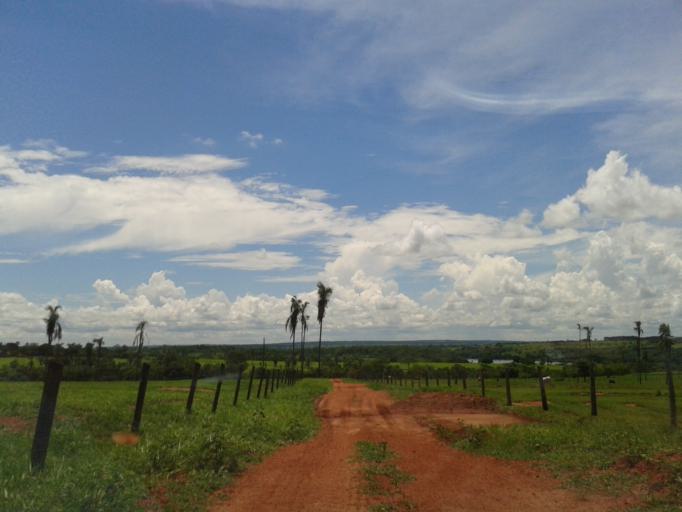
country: BR
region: Minas Gerais
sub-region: Santa Vitoria
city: Santa Vitoria
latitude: -19.1832
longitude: -50.6749
